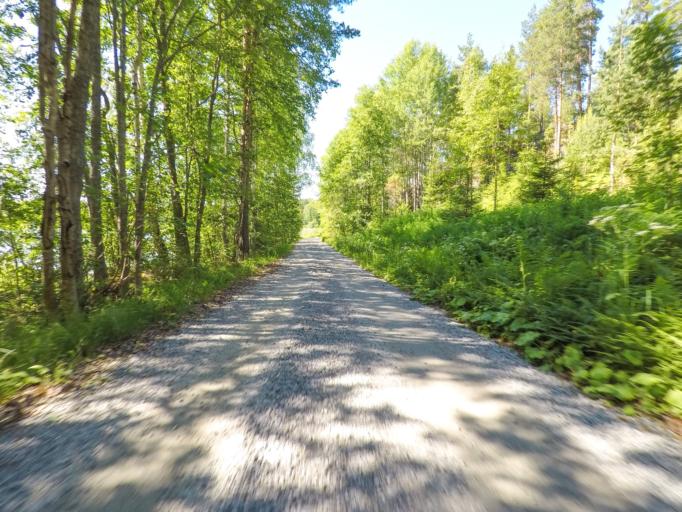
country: FI
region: Northern Savo
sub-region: Varkaus
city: Kangaslampi
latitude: 62.1757
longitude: 28.2386
